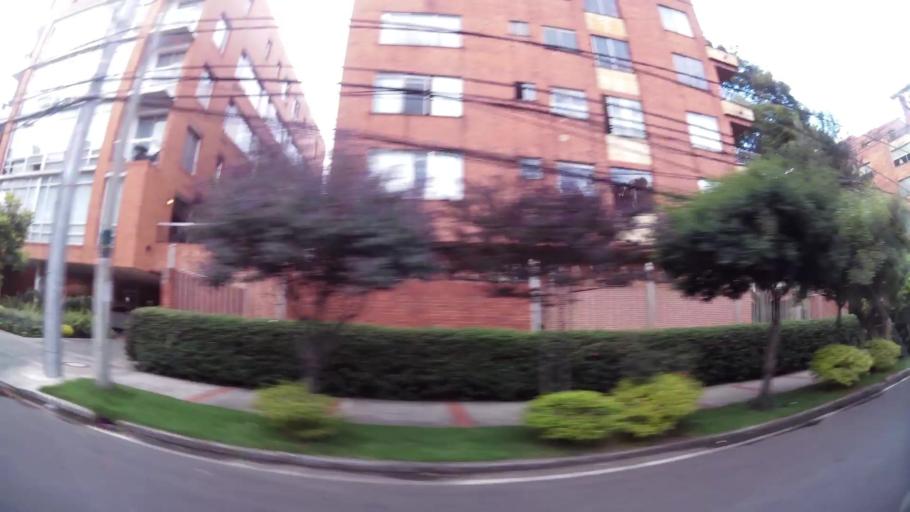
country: CO
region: Bogota D.C.
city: Barrio San Luis
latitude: 4.6907
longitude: -74.0525
